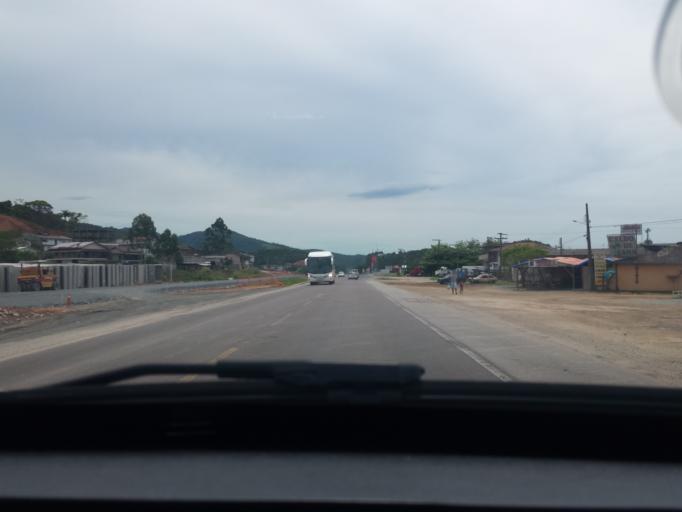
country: BR
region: Santa Catarina
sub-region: Gaspar
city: Gaspar
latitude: -26.9091
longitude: -48.9464
